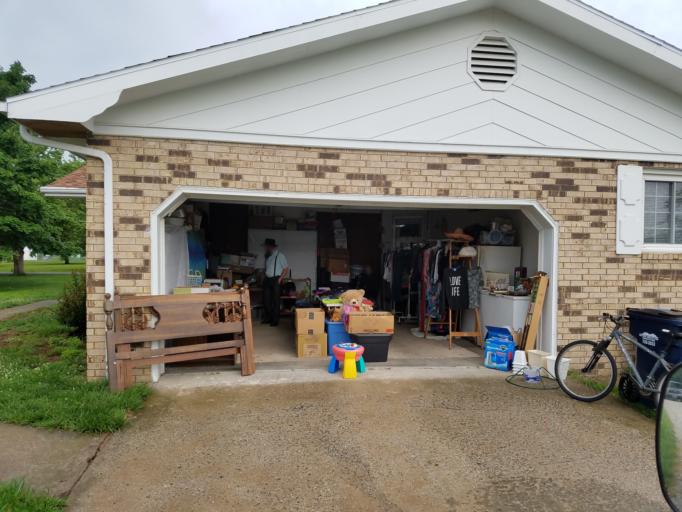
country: US
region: Missouri
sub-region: Dallas County
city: Buffalo
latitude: 37.6407
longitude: -93.1081
